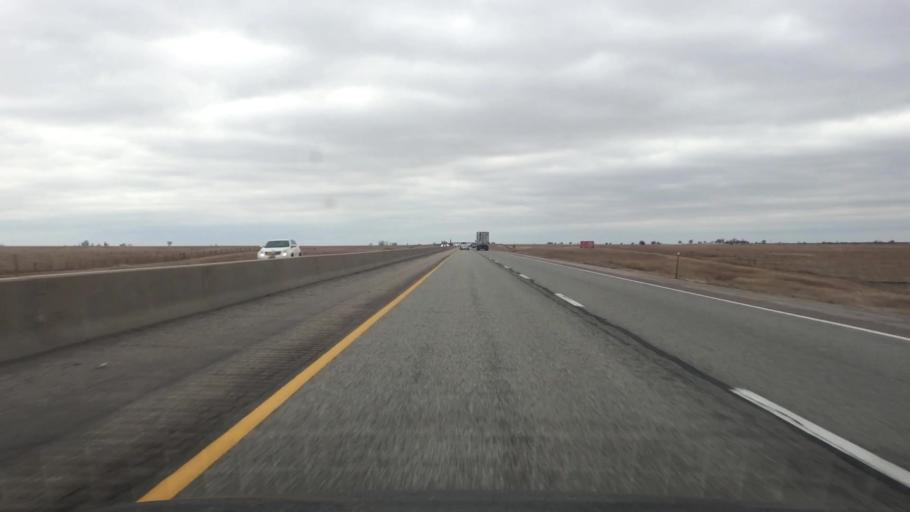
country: US
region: Kansas
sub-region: Butler County
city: El Dorado
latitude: 38.0129
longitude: -96.6769
